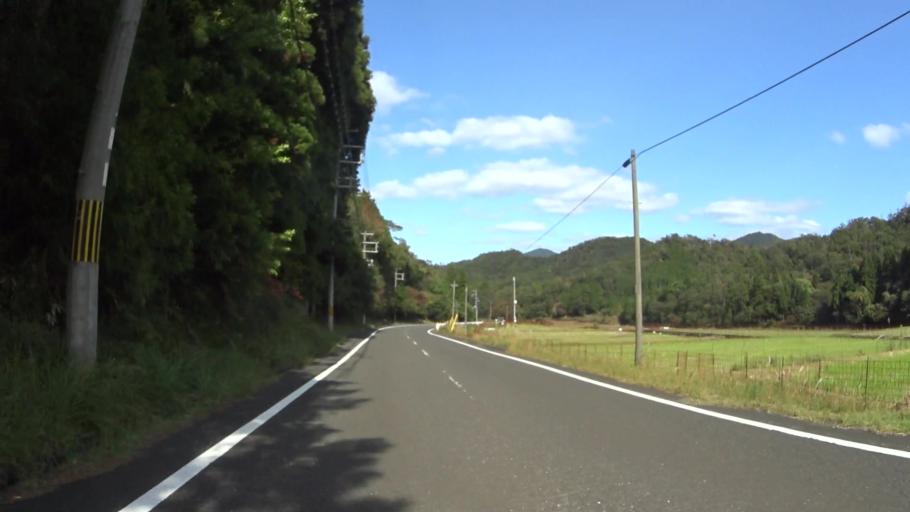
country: JP
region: Hyogo
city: Toyooka
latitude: 35.5544
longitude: 134.9777
